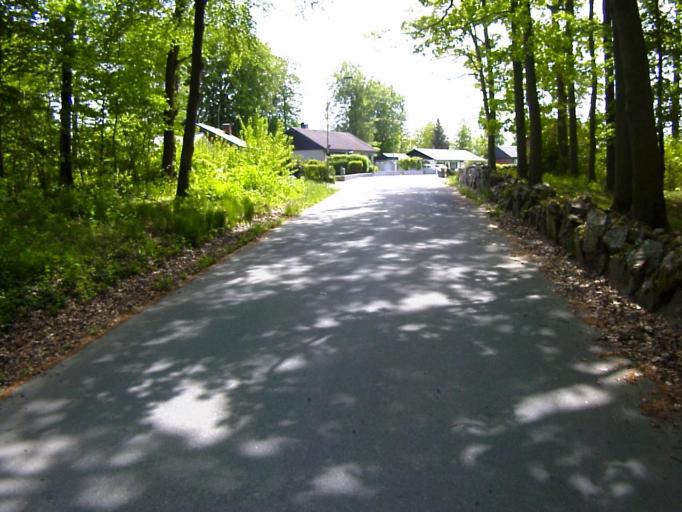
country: SE
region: Skane
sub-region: Kristianstads Kommun
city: Kristianstad
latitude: 56.0757
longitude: 14.0922
